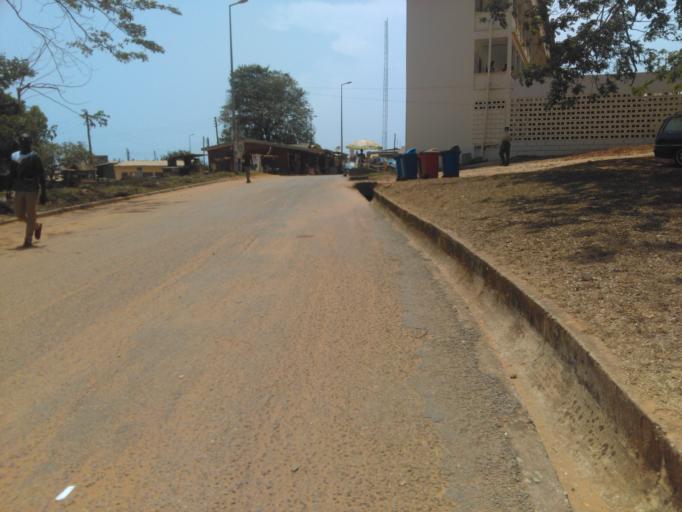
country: GH
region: Central
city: Cape Coast
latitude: 5.1039
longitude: -1.2857
